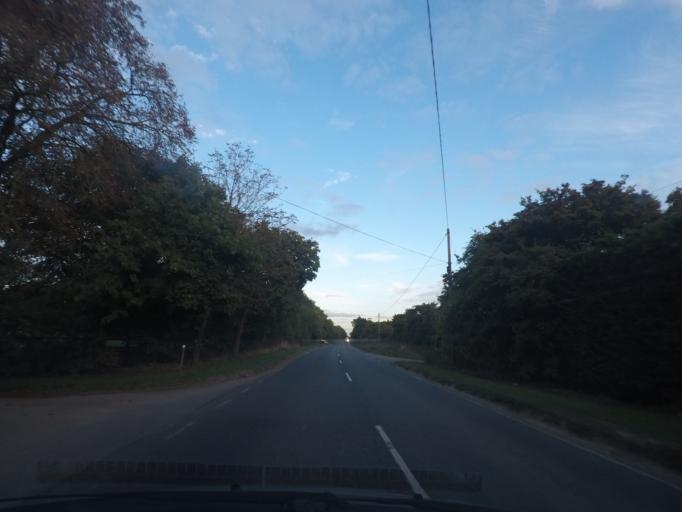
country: GB
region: England
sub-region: Oxfordshire
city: Faringdon
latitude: 51.6535
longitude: -1.5628
